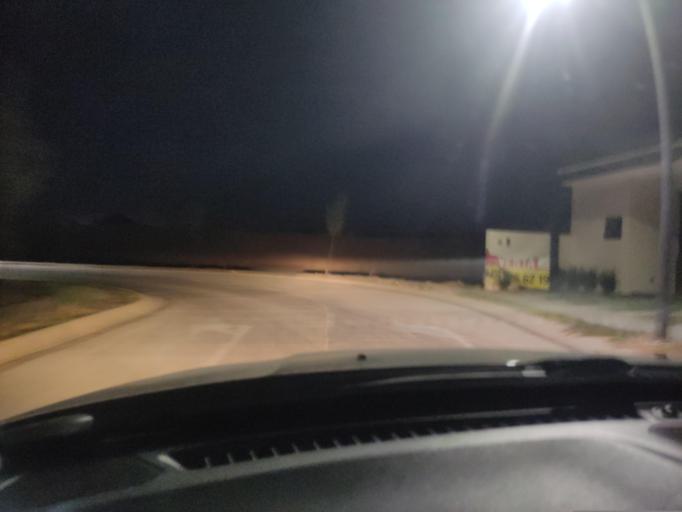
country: MX
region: Guanajuato
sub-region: Leon
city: Ladrilleras del Refugio
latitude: 21.0841
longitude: -101.5601
